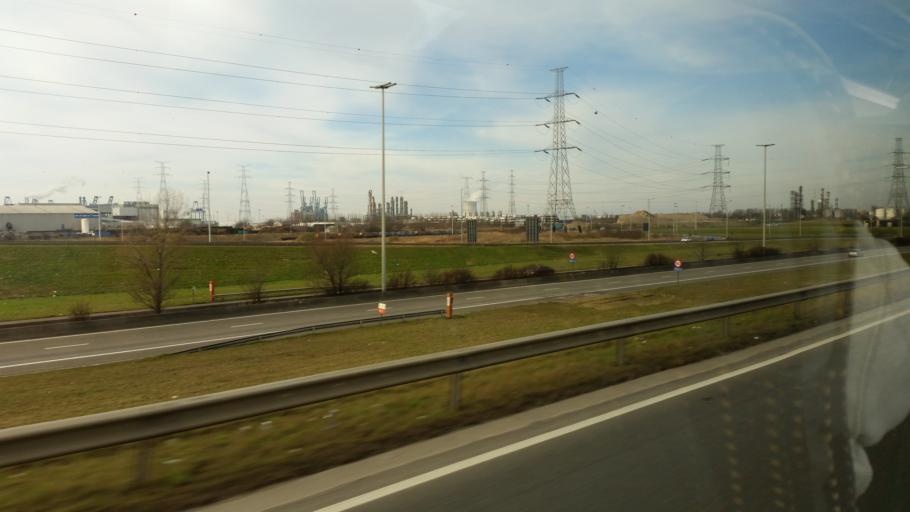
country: BE
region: Flanders
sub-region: Provincie Antwerpen
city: Zwijndrecht
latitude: 51.2789
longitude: 4.2845
